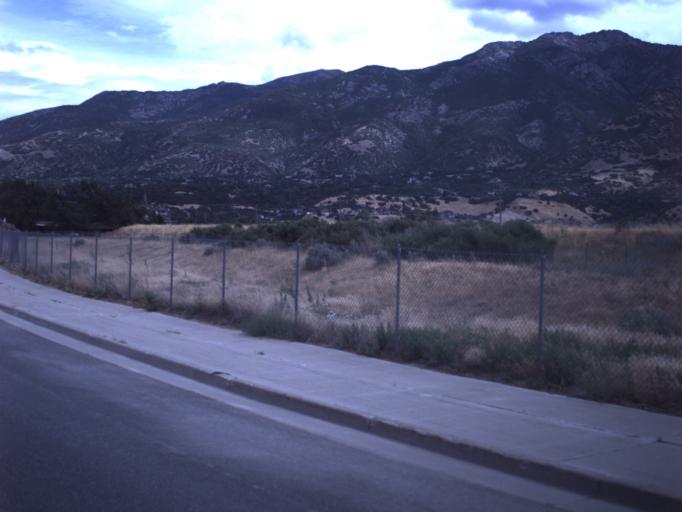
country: US
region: Utah
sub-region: Davis County
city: South Weber
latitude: 41.1297
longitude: -111.9239
